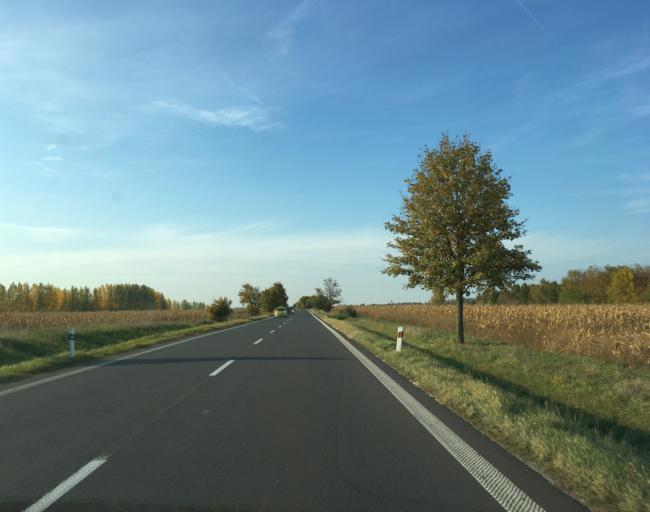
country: SK
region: Nitriansky
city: Surany
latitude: 48.0750
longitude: 18.0857
